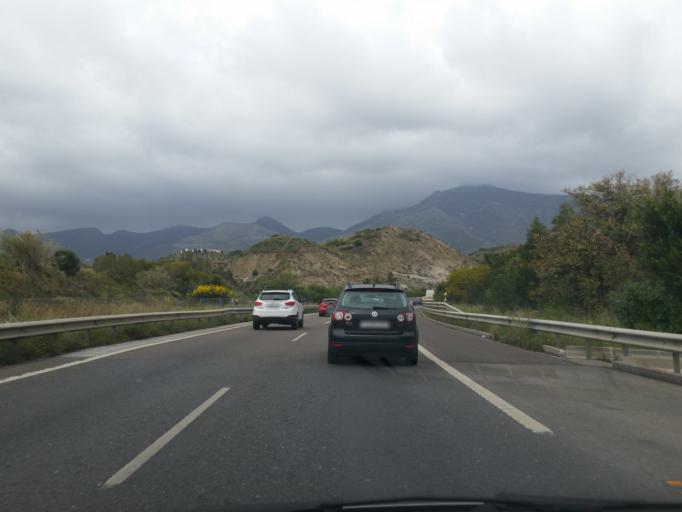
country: ES
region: Andalusia
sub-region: Provincia de Malaga
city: Mijas
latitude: 36.5717
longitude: -4.6228
